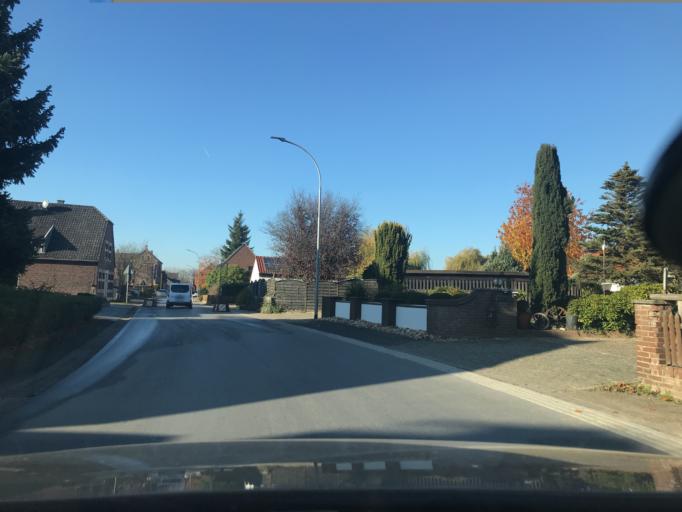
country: DE
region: North Rhine-Westphalia
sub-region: Regierungsbezirk Dusseldorf
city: Wachtendonk
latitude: 51.4357
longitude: 6.4008
